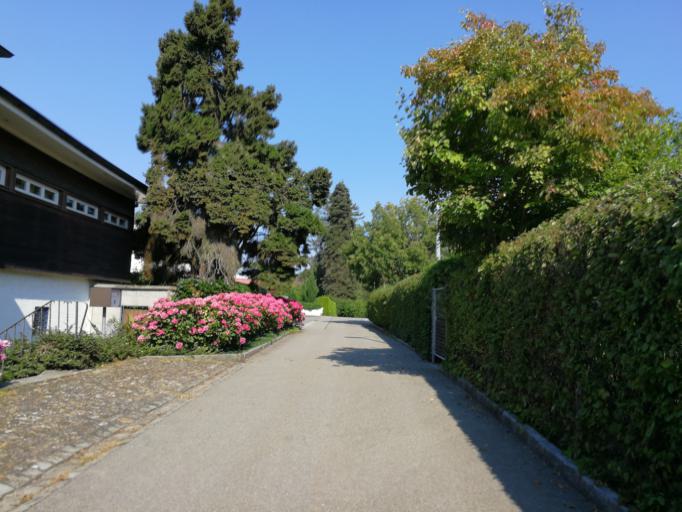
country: CH
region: Zurich
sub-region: Bezirk Meilen
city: Erlenbach / rechts des Dorfbachs oberhalb Bahnlinie
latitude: 47.3045
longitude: 8.6061
